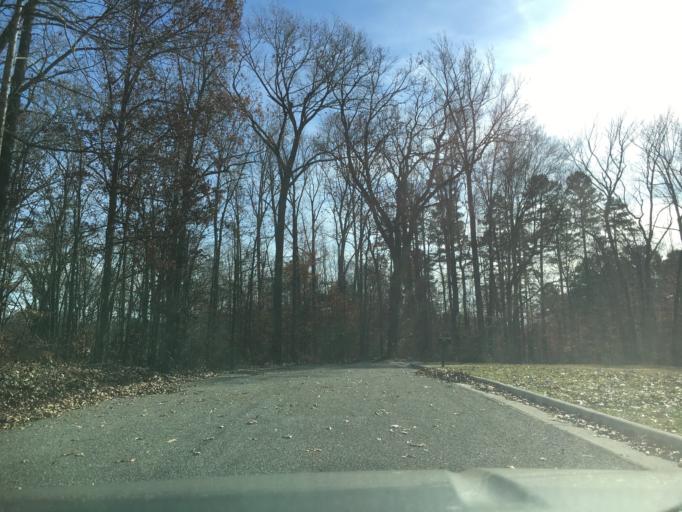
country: US
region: Virginia
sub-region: Halifax County
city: South Boston
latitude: 36.7085
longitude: -78.9174
